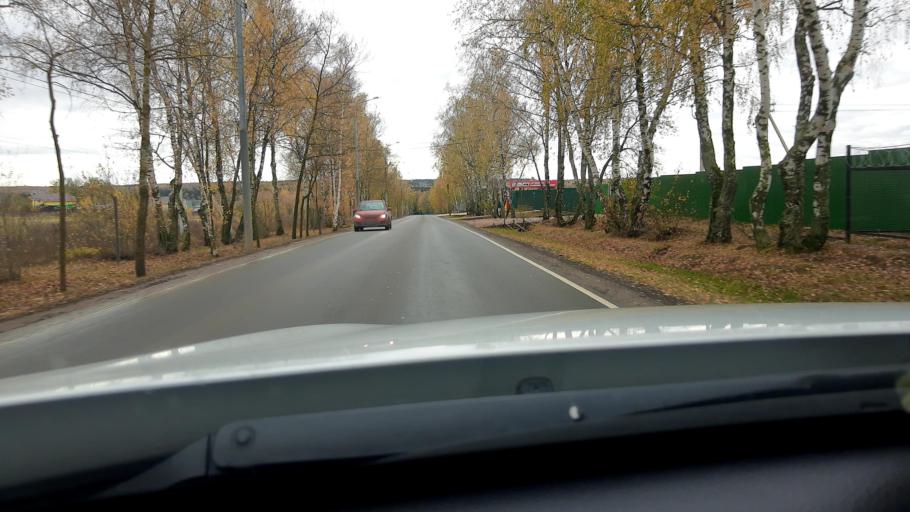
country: RU
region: Moskovskaya
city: Annino
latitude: 55.5705
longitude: 37.2366
